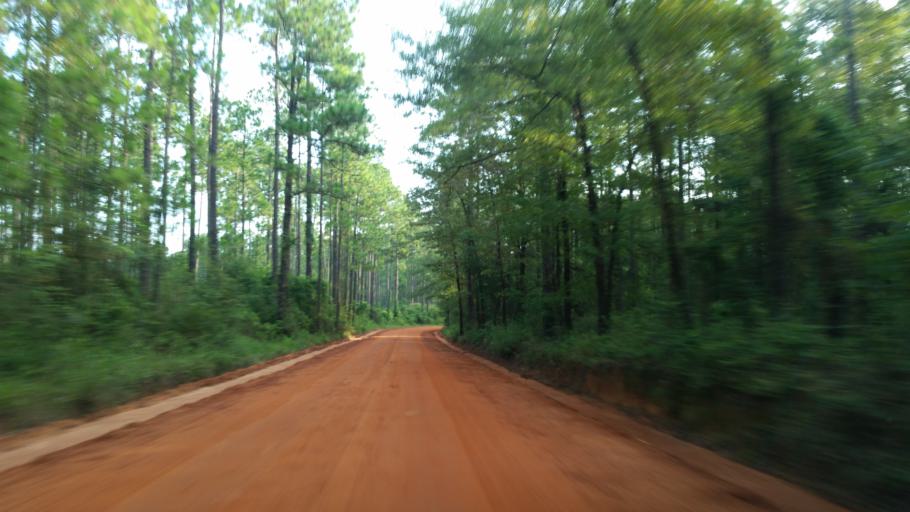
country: US
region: Alabama
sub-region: Escambia County
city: Atmore
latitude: 30.9226
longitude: -87.5756
